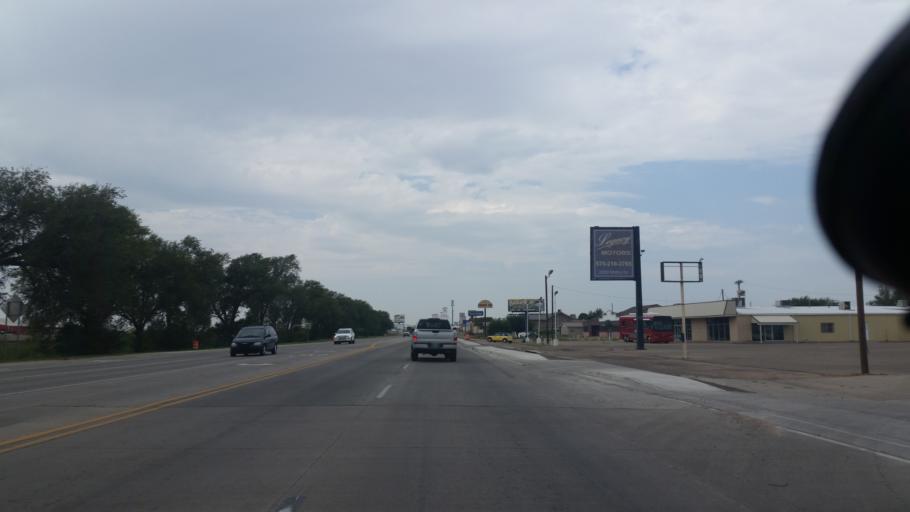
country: US
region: New Mexico
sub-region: Curry County
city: Clovis
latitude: 34.3964
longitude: -103.1790
